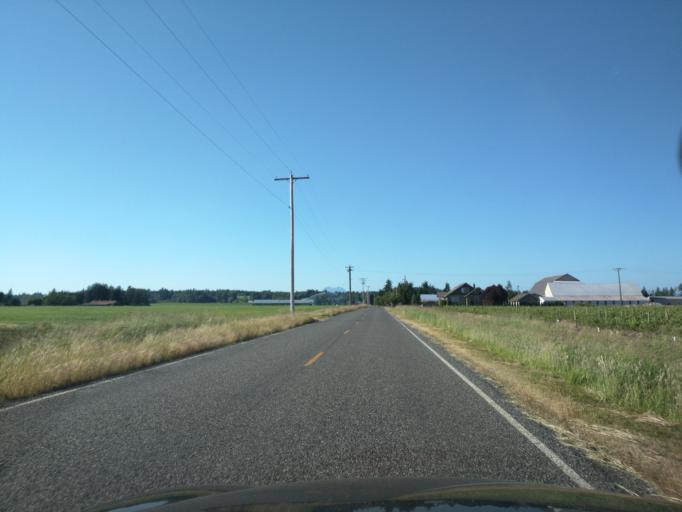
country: US
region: Washington
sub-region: Whatcom County
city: Lynden
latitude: 48.9895
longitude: -122.4519
